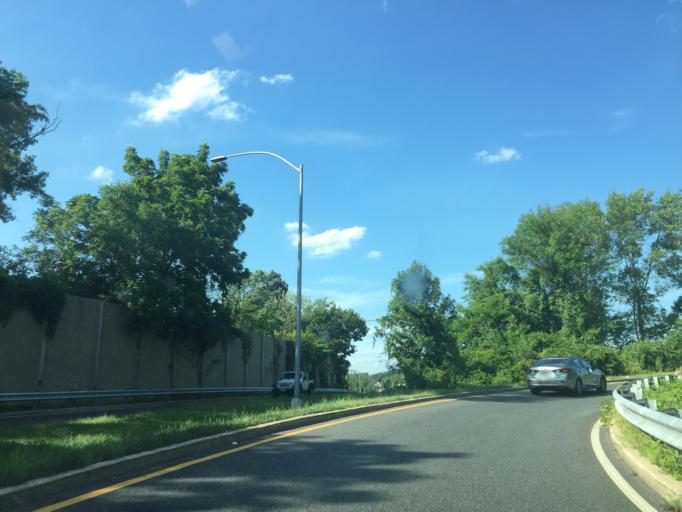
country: US
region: Maryland
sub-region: Baltimore County
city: Mays Chapel
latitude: 39.4389
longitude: -76.6352
